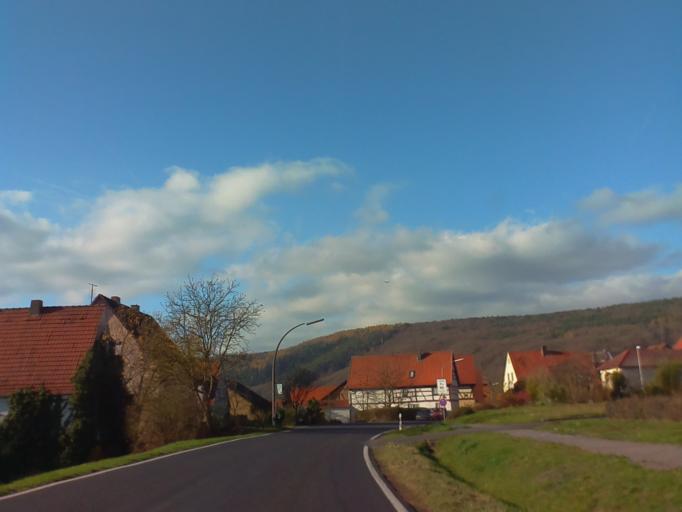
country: DE
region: Bavaria
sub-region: Regierungsbezirk Unterfranken
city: Bad Bocklet
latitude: 50.2793
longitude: 10.0839
